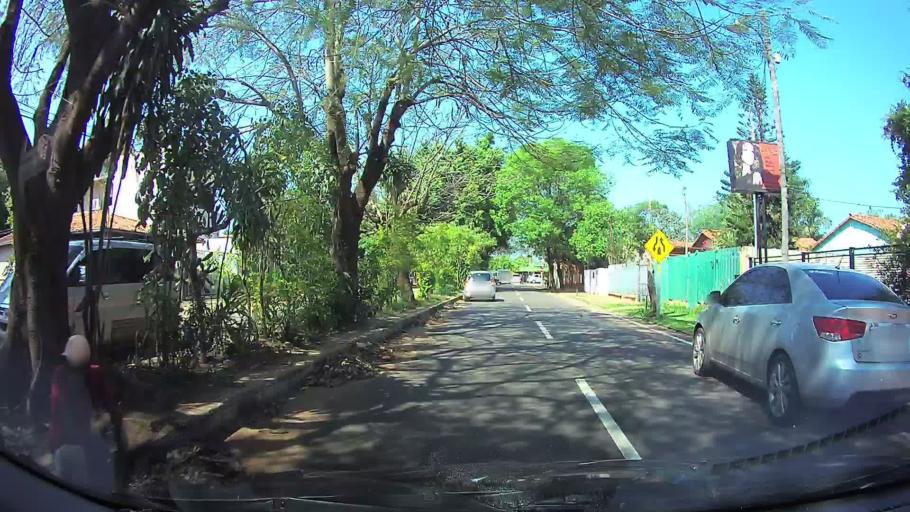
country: PY
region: Central
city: Limpio
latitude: -25.2361
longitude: -57.4759
